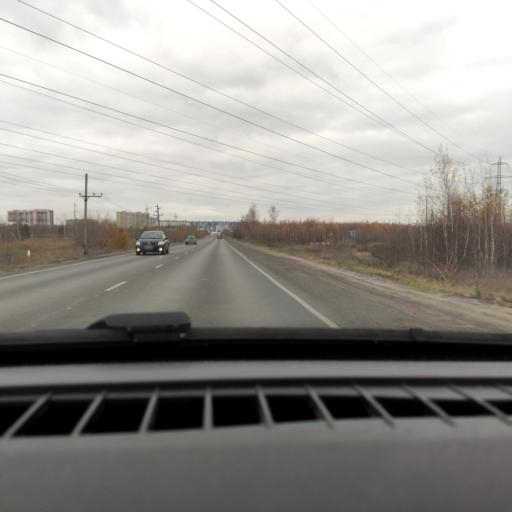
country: RU
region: Voronezj
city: Maslovka
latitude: 51.5817
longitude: 39.2615
